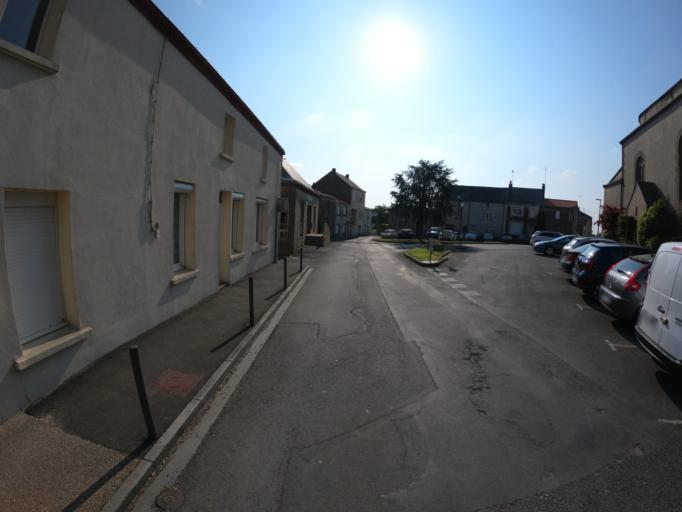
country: FR
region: Pays de la Loire
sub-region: Departement de Maine-et-Loire
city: La Romagne
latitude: 47.0622
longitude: -1.0209
